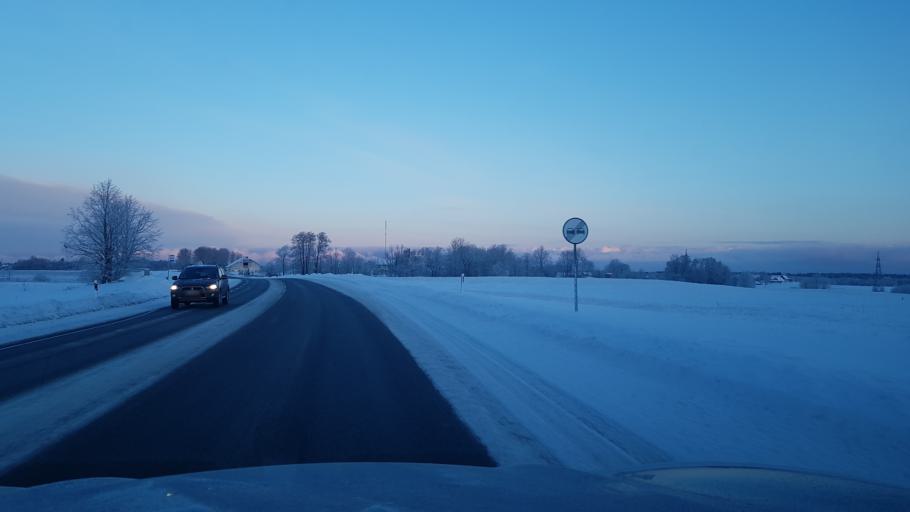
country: EE
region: Ida-Virumaa
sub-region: Narva-Joesuu linn
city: Narva-Joesuu
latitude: 59.3963
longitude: 28.0783
